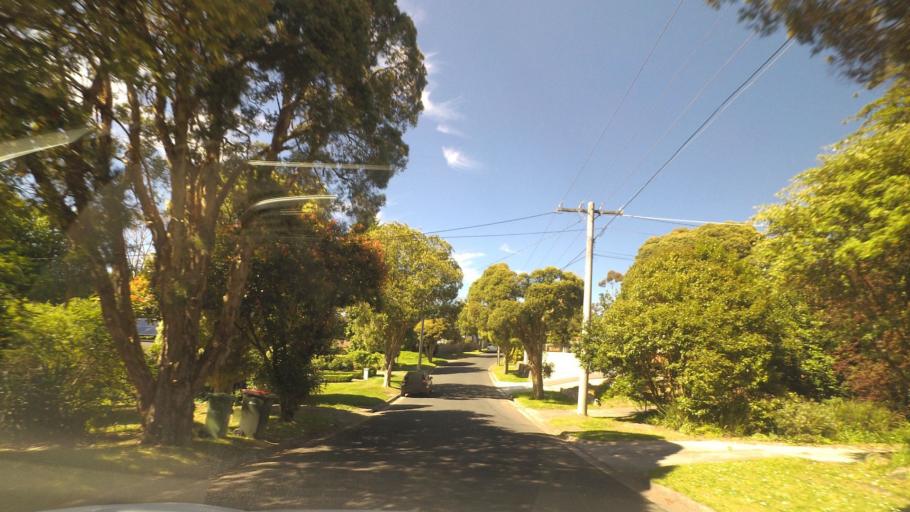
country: AU
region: Victoria
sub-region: Maroondah
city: Ringwood East
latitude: -37.8248
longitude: 145.2551
